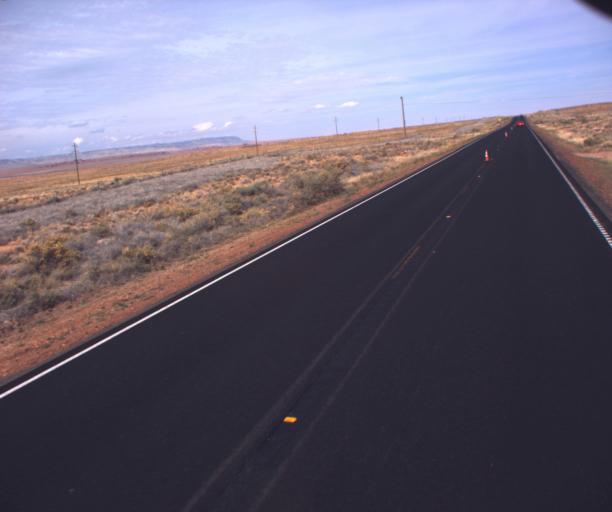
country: US
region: Arizona
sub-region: Apache County
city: Chinle
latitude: 36.0566
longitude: -109.6087
